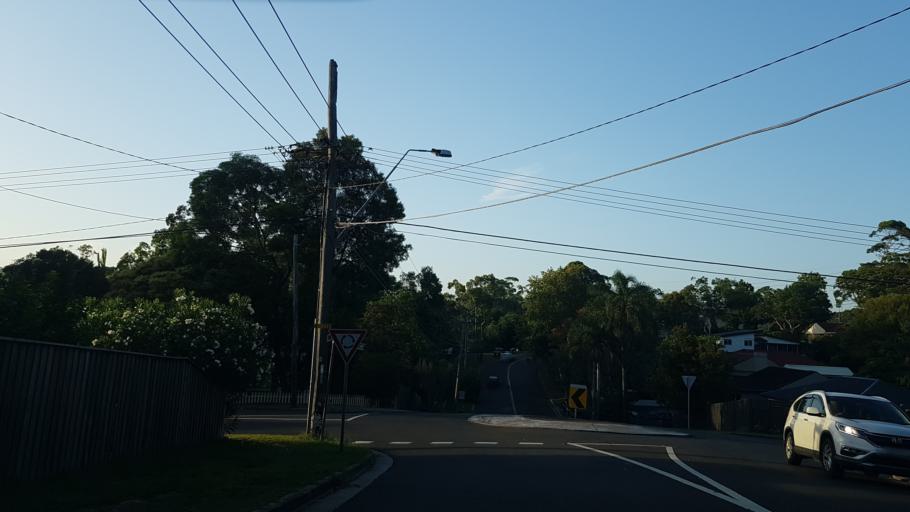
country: AU
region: New South Wales
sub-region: Warringah
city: Narraweena
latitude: -33.7348
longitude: 151.2727
